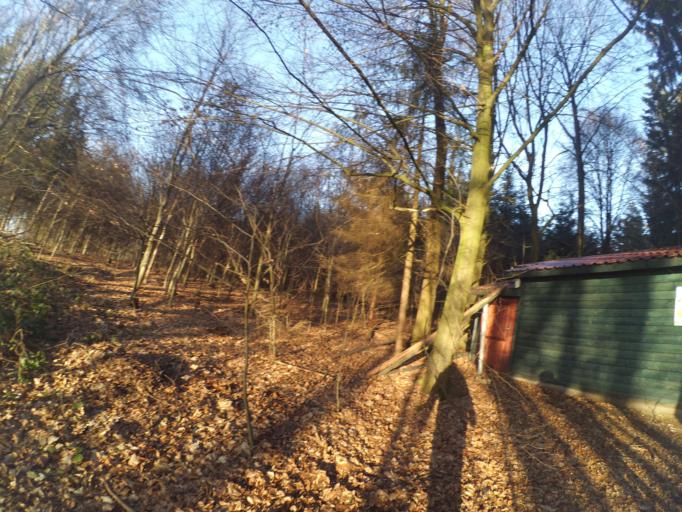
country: DE
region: Bavaria
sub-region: Swabia
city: Guenzburg
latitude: 48.4467
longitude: 10.3021
